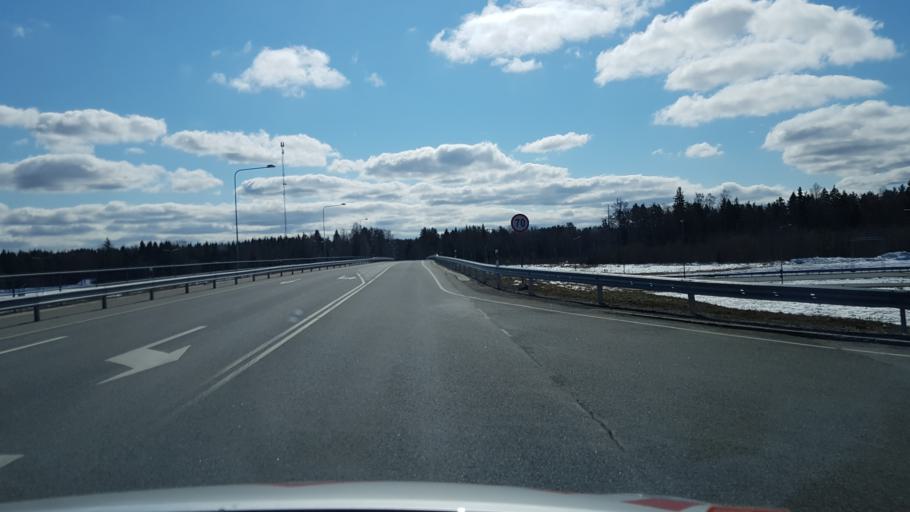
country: EE
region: Laeaene-Virumaa
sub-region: Kadrina vald
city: Kadrina
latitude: 59.4642
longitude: 26.0013
